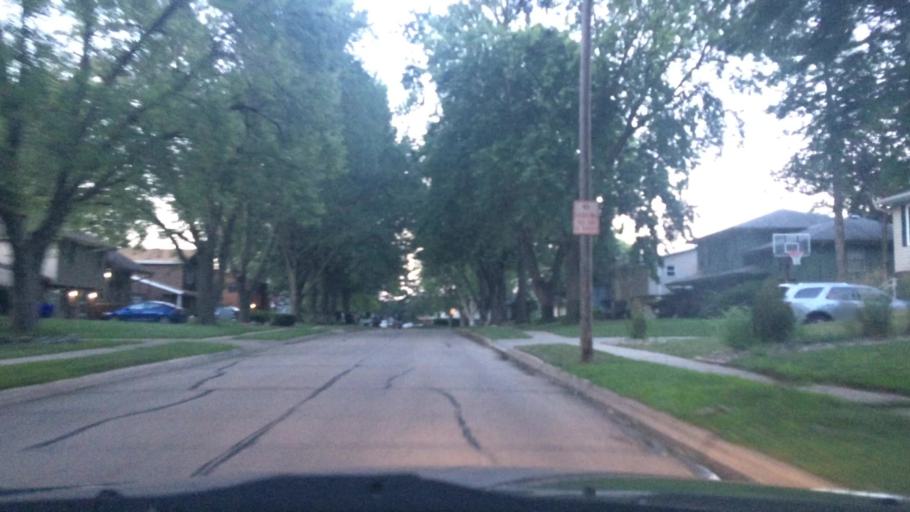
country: US
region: Nebraska
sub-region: Douglas County
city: Ralston
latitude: 41.1898
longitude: -96.0519
